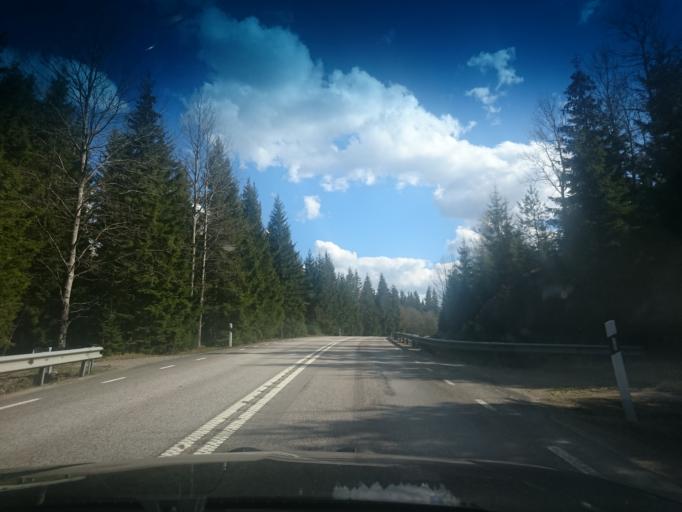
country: SE
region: Joenkoeping
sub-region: Vetlanda Kommun
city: Vetlanda
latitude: 57.2694
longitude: 15.1279
